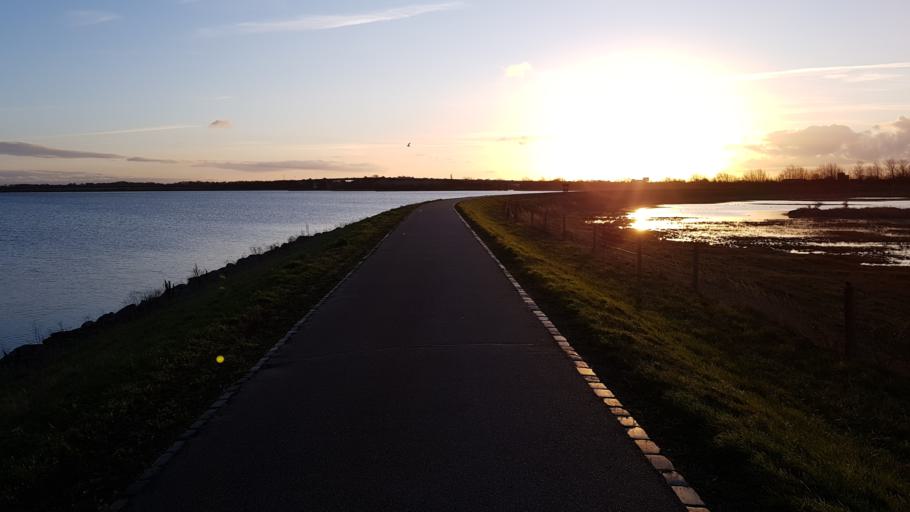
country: DK
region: Capital Region
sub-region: Hvidovre Kommune
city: Hvidovre
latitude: 55.6189
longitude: 12.4955
